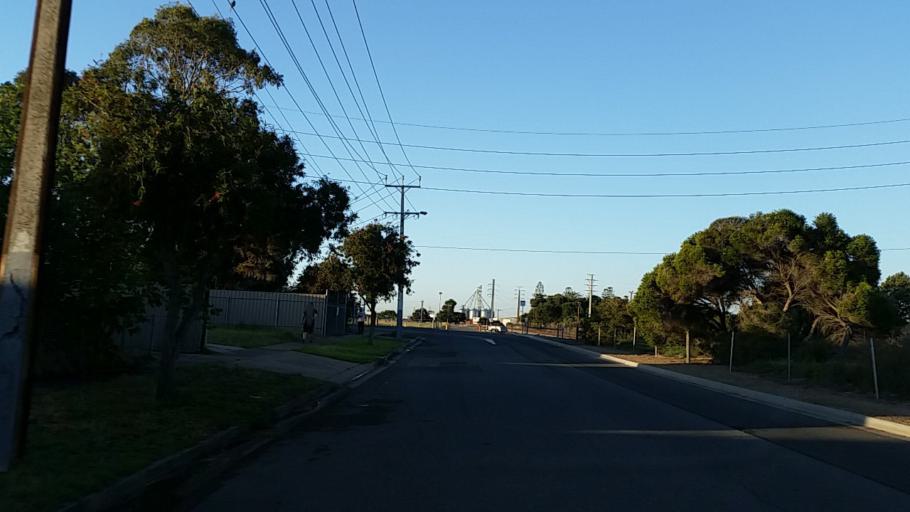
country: AU
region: South Australia
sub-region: Port Adelaide Enfield
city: Birkenhead
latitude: -34.7969
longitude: 138.5048
